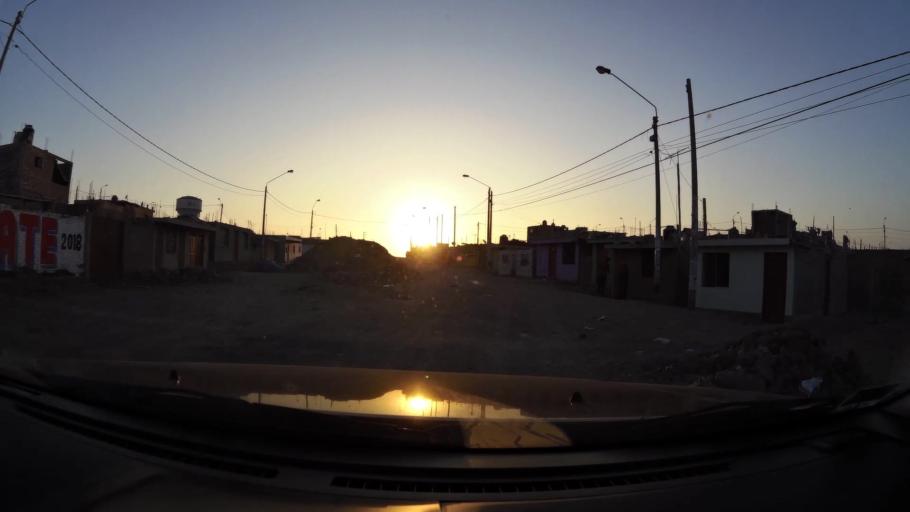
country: PE
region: Ica
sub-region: Provincia de Pisco
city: San Clemente
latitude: -13.6754
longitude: -76.1549
